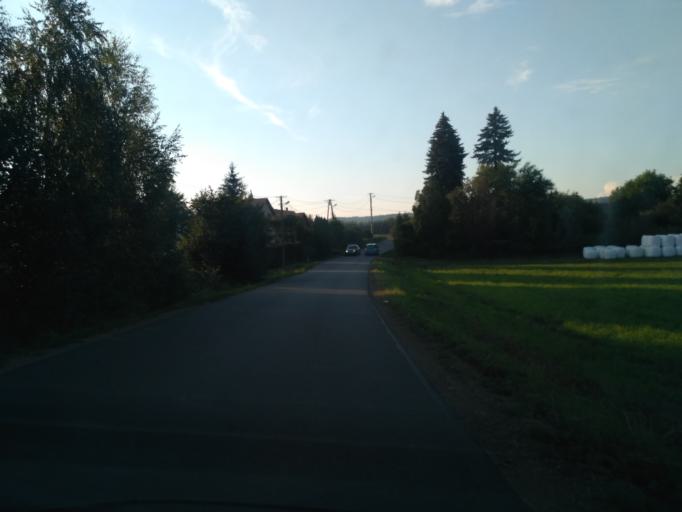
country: PL
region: Subcarpathian Voivodeship
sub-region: Powiat krosnienski
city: Korczyna
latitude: 49.7077
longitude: 21.8287
